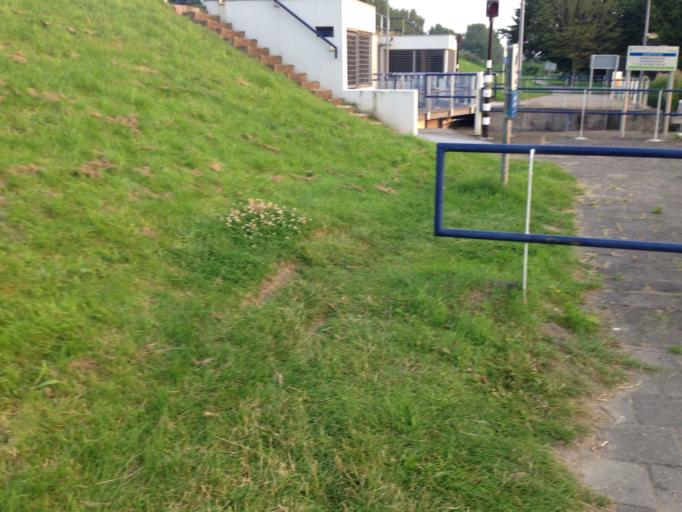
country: NL
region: Flevoland
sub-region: Gemeente Almere
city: Almere Stad
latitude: 52.4072
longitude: 5.2321
